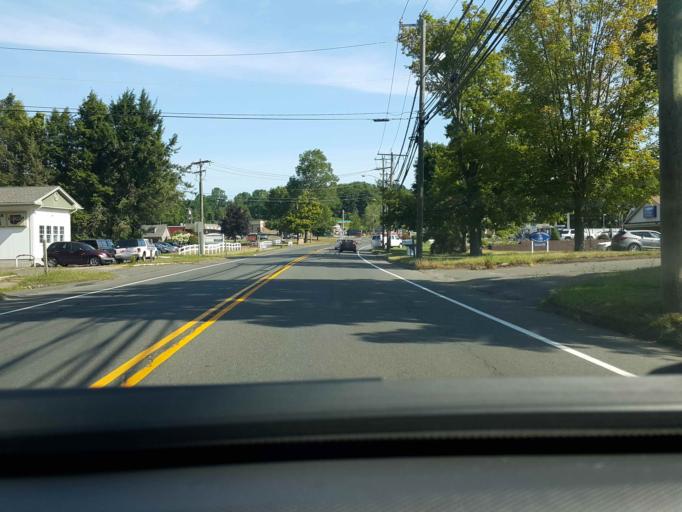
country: US
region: Connecticut
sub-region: Middlesex County
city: Durham
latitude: 41.4836
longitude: -72.6819
